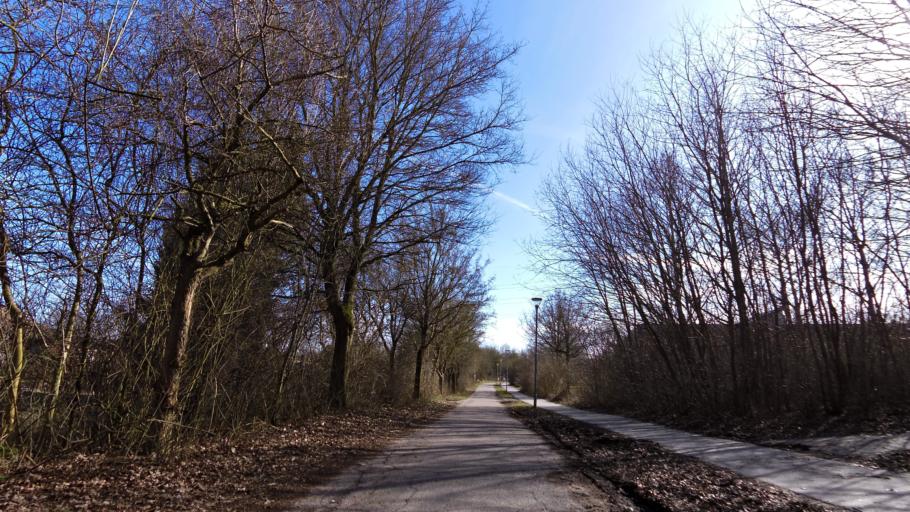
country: DK
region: Central Jutland
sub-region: Arhus Kommune
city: Stavtrup
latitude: 56.1671
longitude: 10.1393
